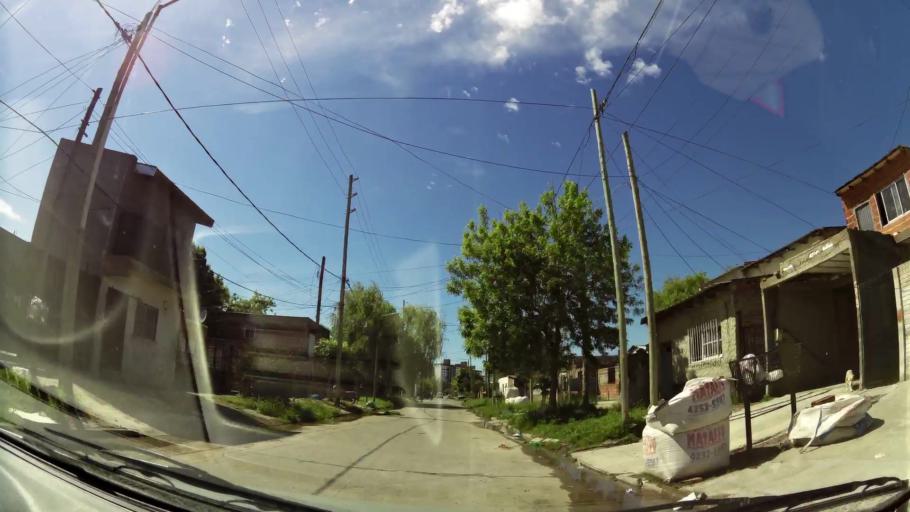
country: AR
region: Buenos Aires
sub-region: Partido de Quilmes
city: Quilmes
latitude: -34.6878
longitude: -58.3054
